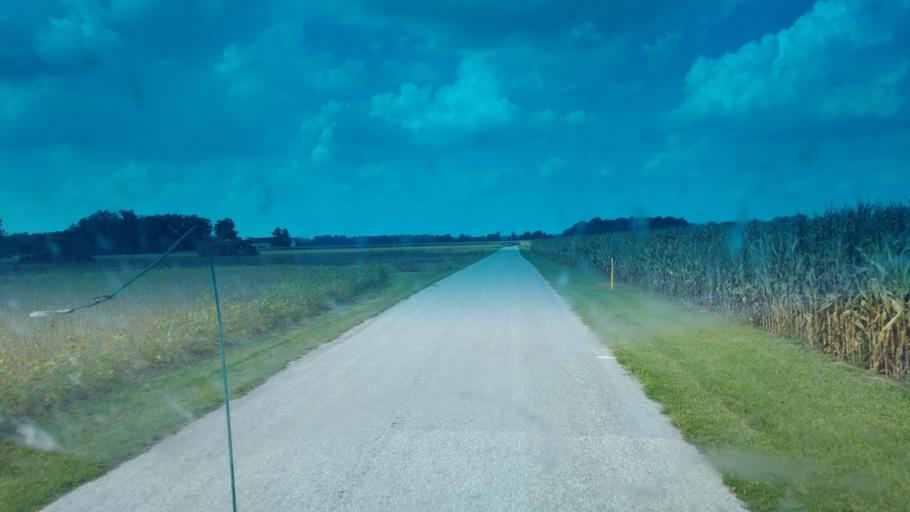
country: US
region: Ohio
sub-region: Hardin County
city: Kenton
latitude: 40.7283
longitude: -83.6145
